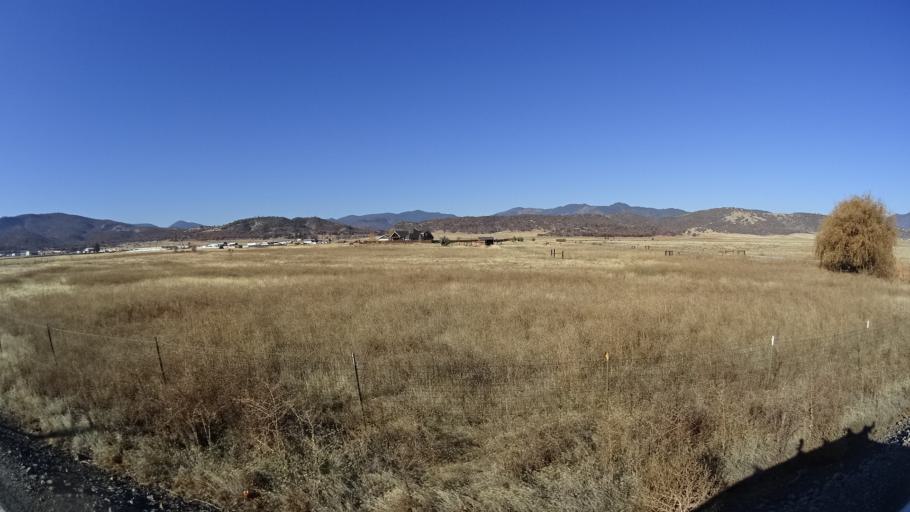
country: US
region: California
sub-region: Siskiyou County
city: Yreka
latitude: 41.7142
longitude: -122.5935
